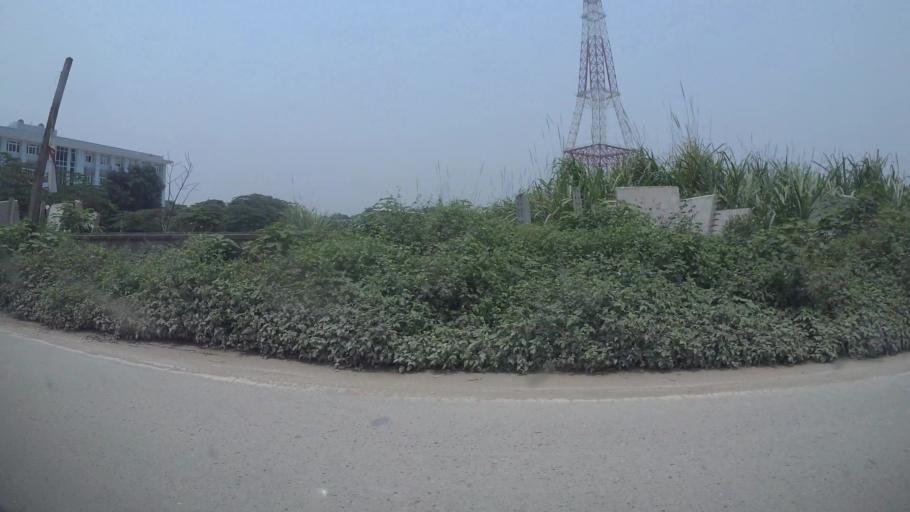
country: VN
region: Ha Noi
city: Ha Dong
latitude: 21.0006
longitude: 105.7654
